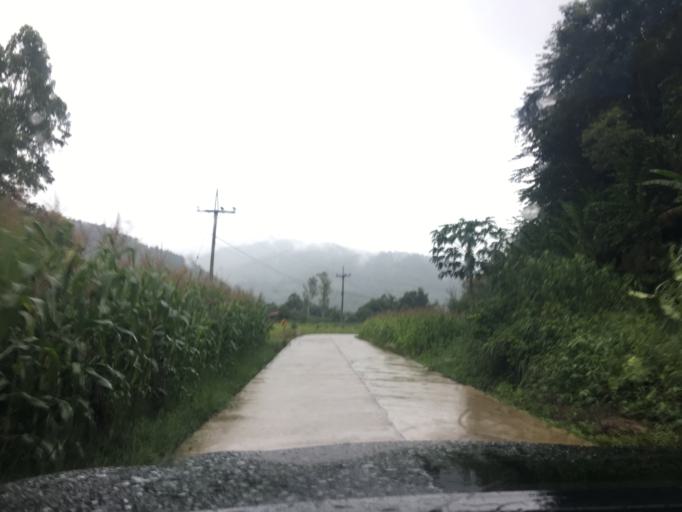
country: TH
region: Chiang Rai
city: Chiang Khong
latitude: 20.2981
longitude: 100.2566
